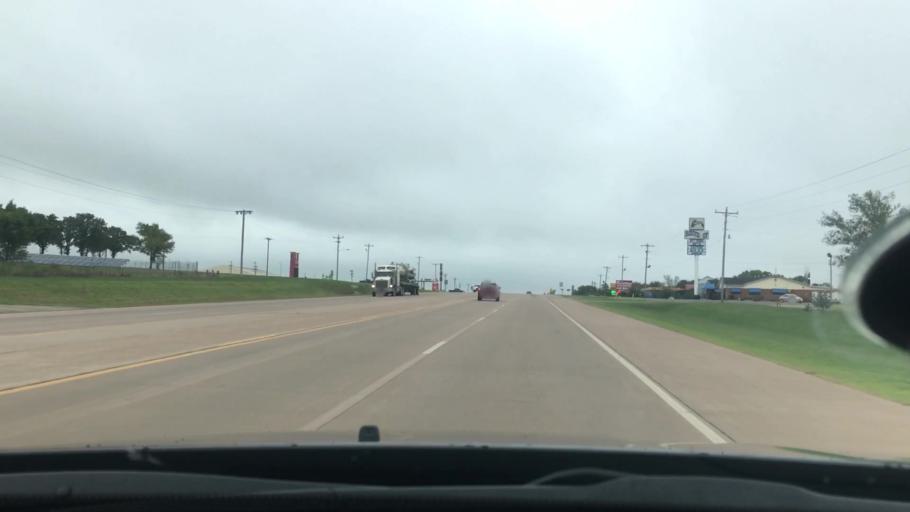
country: US
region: Oklahoma
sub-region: Lincoln County
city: Prague
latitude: 35.3782
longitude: -96.6714
